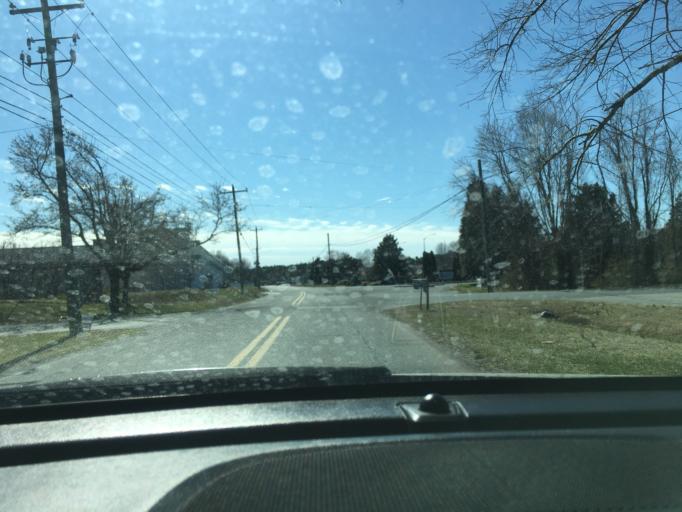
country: US
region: Maryland
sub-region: Wicomico County
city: Delmar
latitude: 38.4045
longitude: -75.5711
